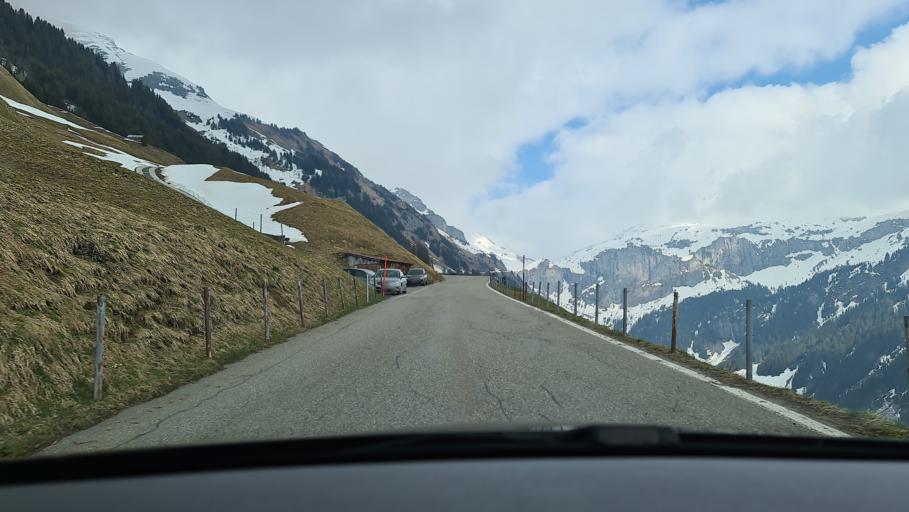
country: CH
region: Schwyz
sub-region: Bezirk Schwyz
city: Muotathal
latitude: 46.8712
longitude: 8.7821
